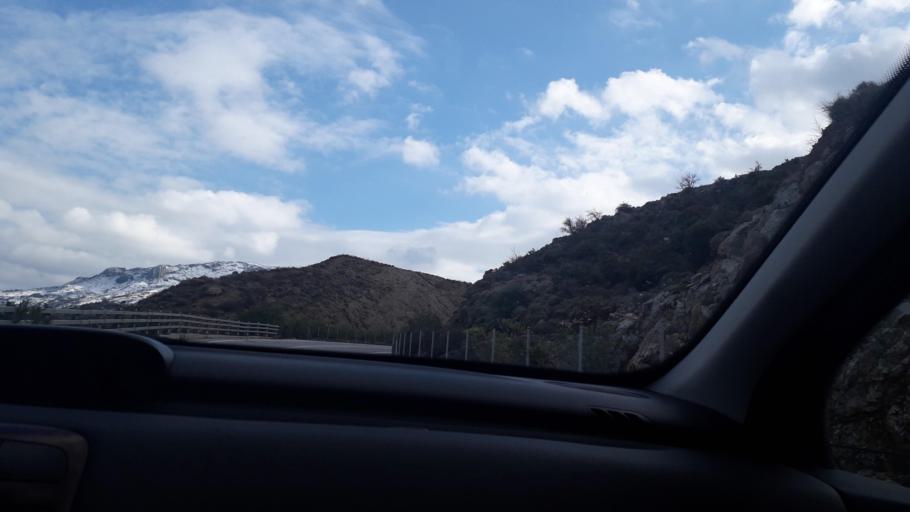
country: GR
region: Crete
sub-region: Nomos Rethymnis
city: Agia Foteini
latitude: 35.2653
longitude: 24.5649
